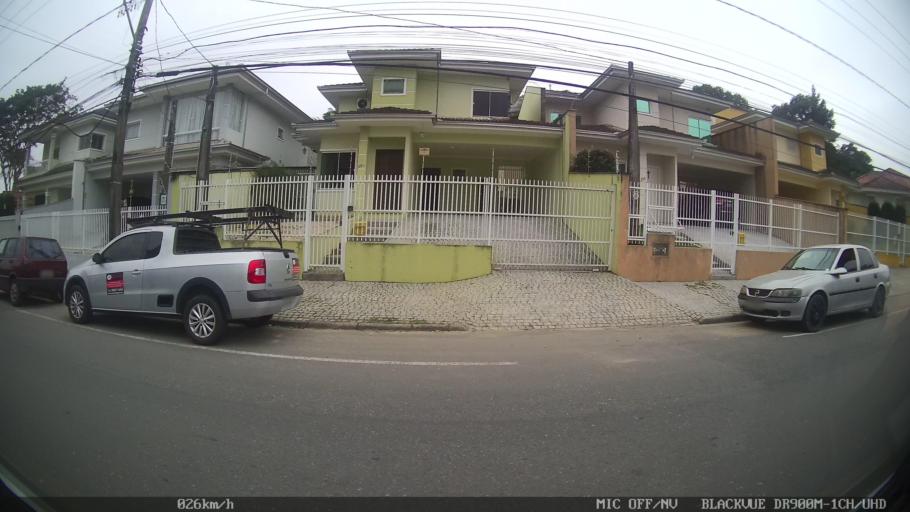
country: BR
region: Santa Catarina
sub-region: Joinville
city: Joinville
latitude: -26.2713
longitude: -48.8434
